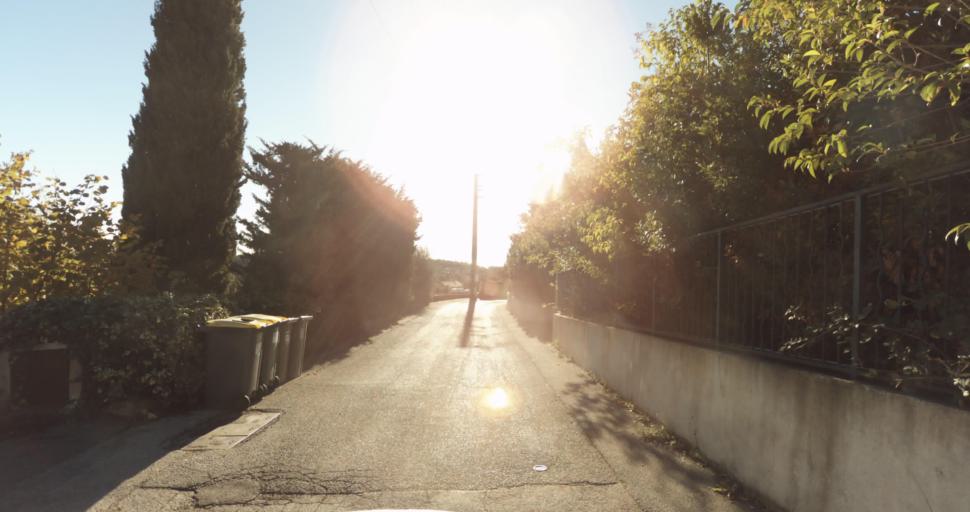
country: FR
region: Provence-Alpes-Cote d'Azur
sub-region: Departement des Alpes-Maritimes
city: Vence
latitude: 43.7261
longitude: 7.0850
